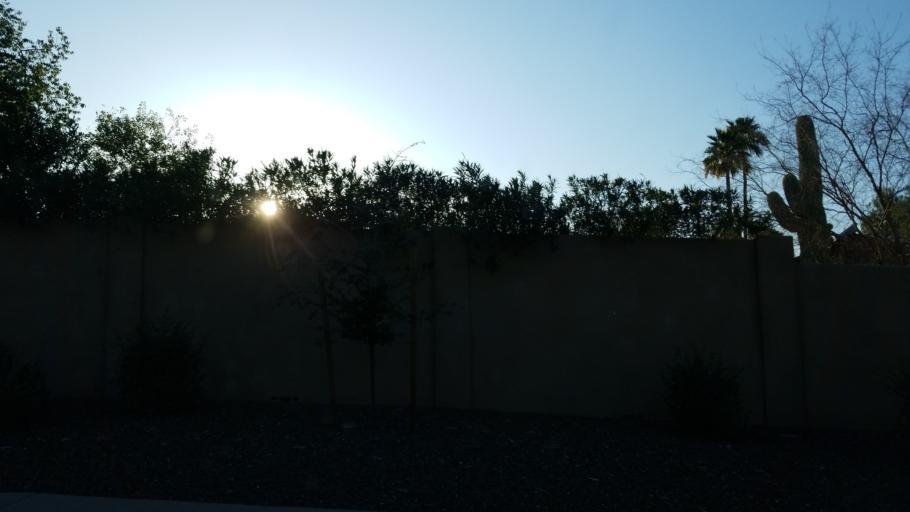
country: US
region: Arizona
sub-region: Maricopa County
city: Paradise Valley
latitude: 33.5801
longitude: -111.9174
